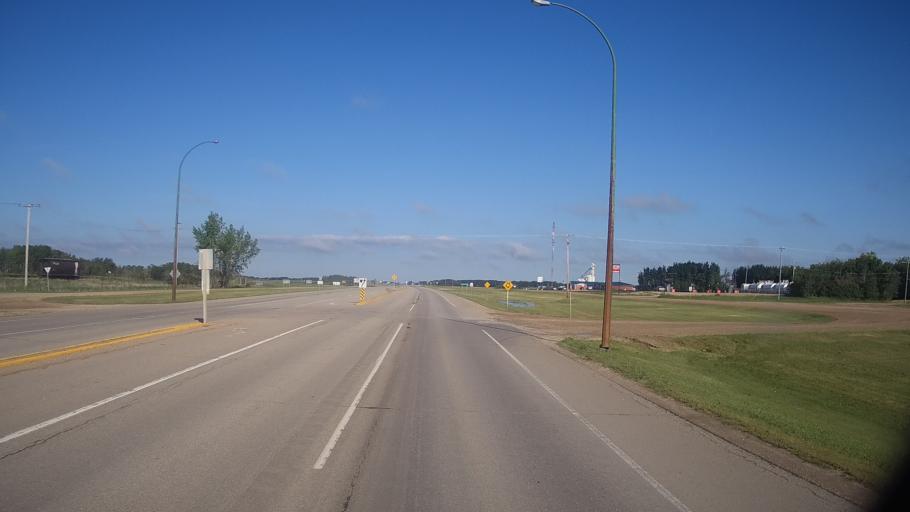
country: CA
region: Saskatchewan
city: Lanigan
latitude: 51.8473
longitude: -105.0419
